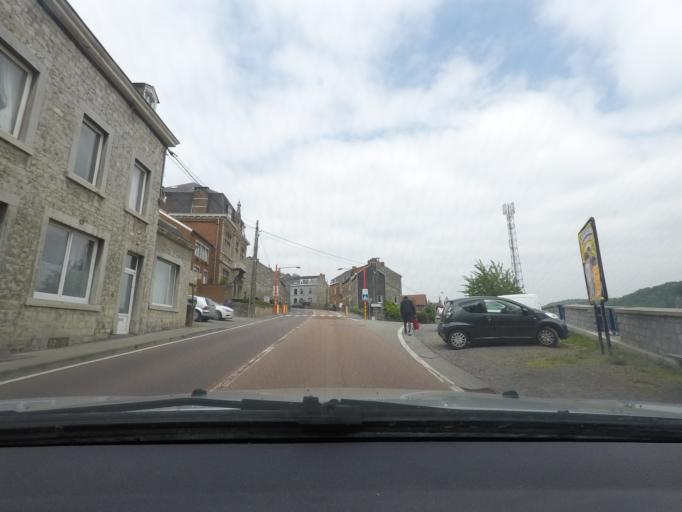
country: BE
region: Wallonia
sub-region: Province de Namur
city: Noville-les-Bois
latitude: 50.4704
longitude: 4.9972
